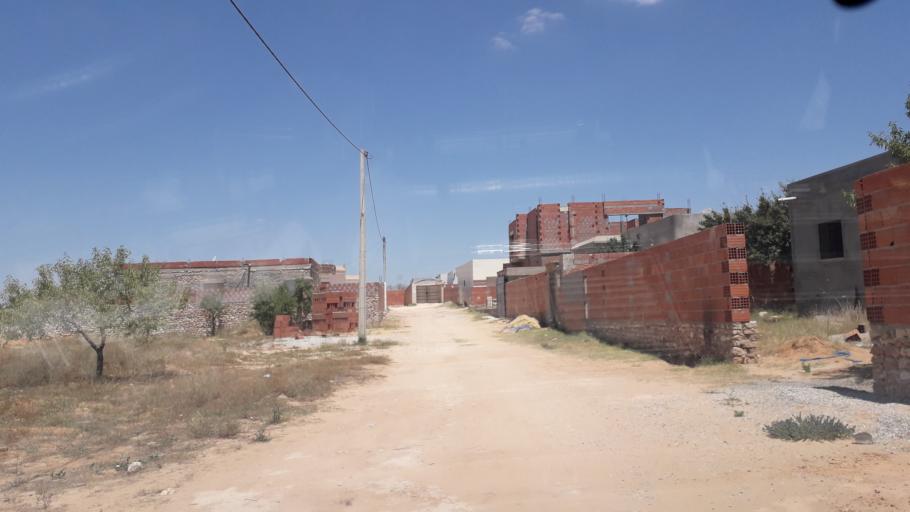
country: TN
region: Safaqis
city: Al Qarmadah
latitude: 34.8298
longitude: 10.7759
